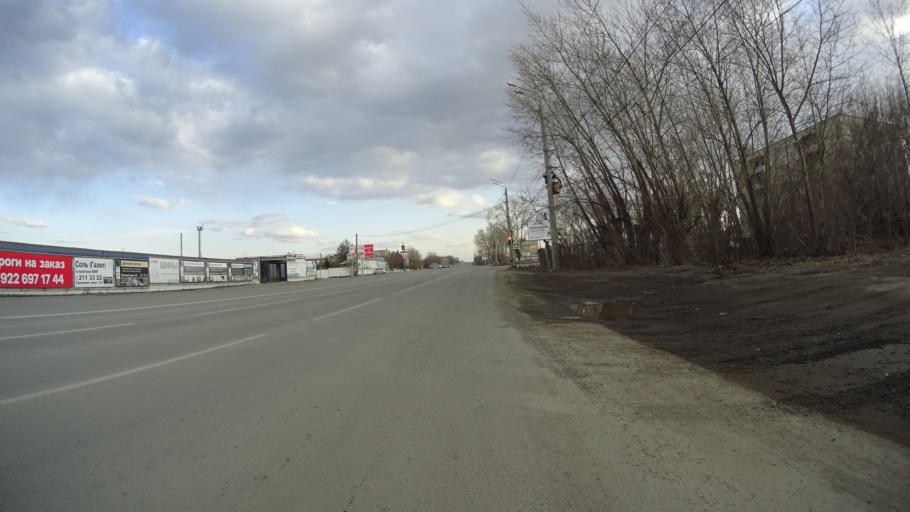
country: RU
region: Chelyabinsk
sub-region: Gorod Chelyabinsk
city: Chelyabinsk
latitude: 55.1079
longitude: 61.3869
